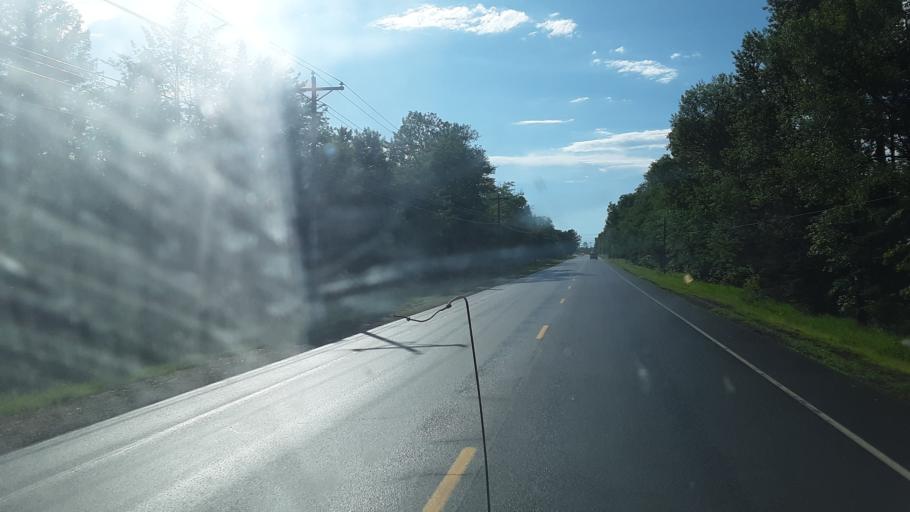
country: US
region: Maine
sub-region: Washington County
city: Calais
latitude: 45.2101
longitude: -67.5405
